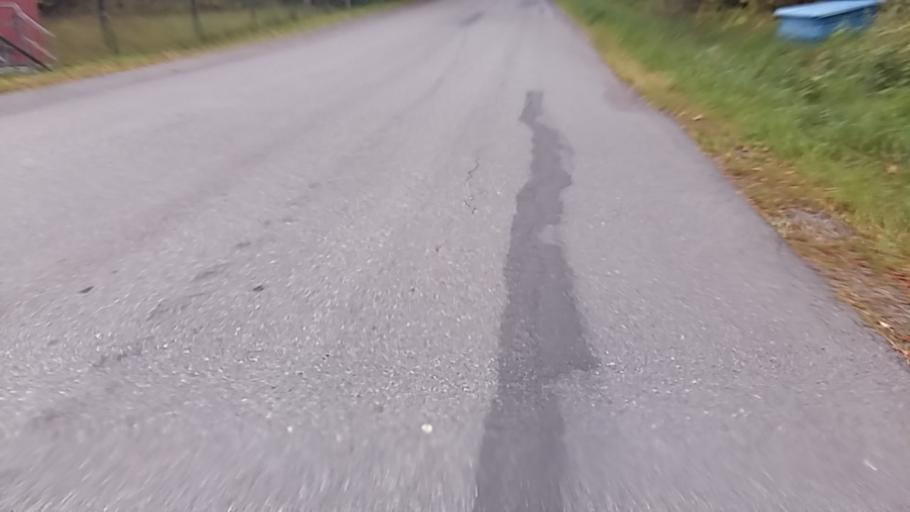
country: SE
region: Joenkoeping
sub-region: Jonkopings Kommun
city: Taberg
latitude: 57.7044
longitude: 14.1143
